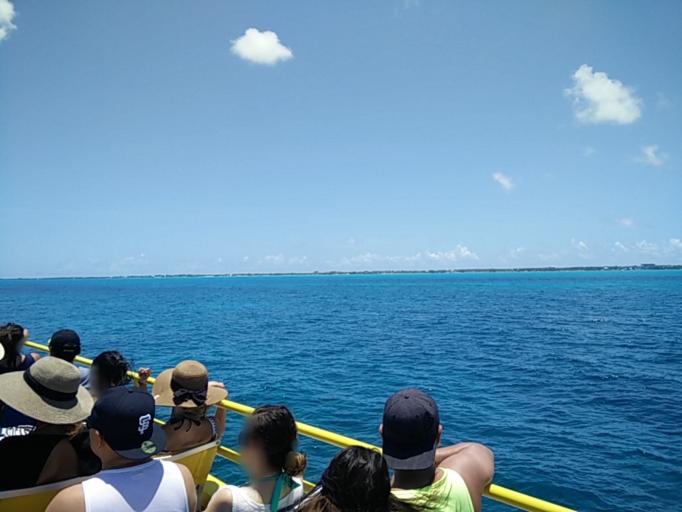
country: MX
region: Quintana Roo
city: Isla Mujeres
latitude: 21.2014
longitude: -86.7595
